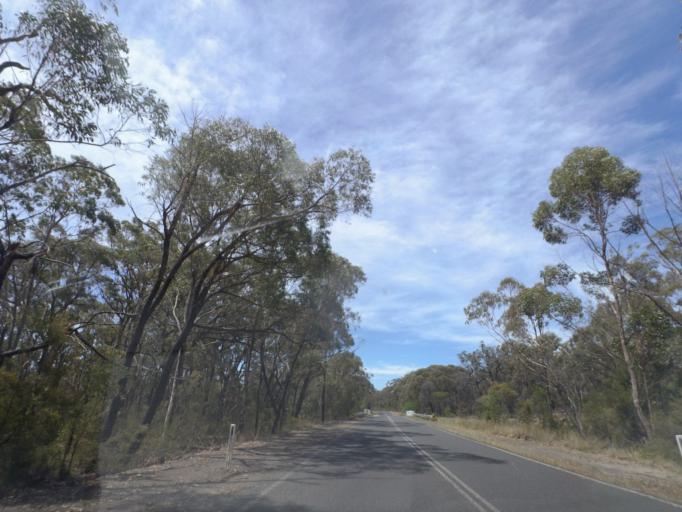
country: AU
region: New South Wales
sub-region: Wollondilly
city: Buxton
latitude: -34.3321
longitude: 150.5601
